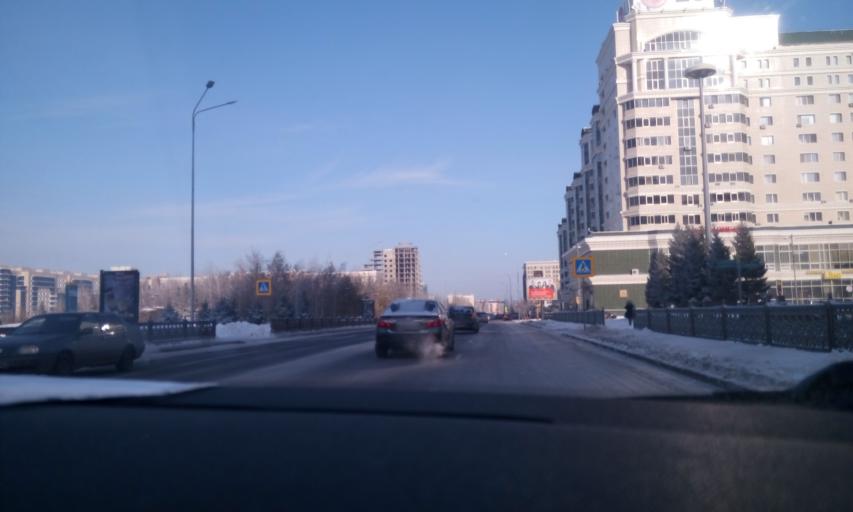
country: KZ
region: Astana Qalasy
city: Astana
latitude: 51.1276
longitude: 71.4323
